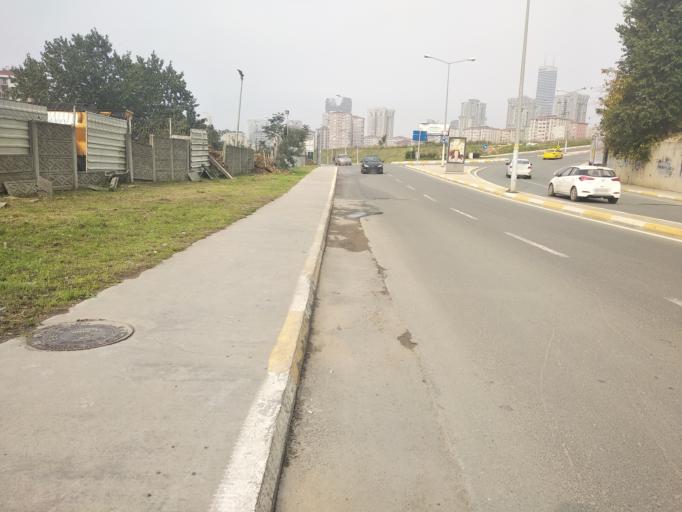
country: TR
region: Istanbul
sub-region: Atasehir
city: Atasehir
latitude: 40.9818
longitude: 29.1292
